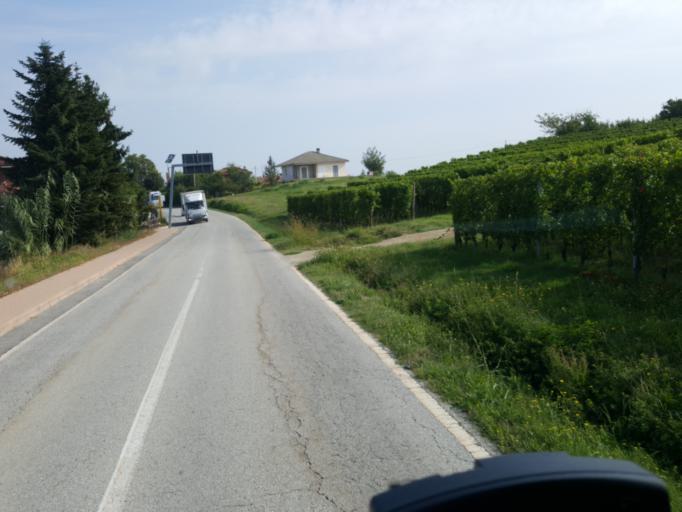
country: IT
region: Piedmont
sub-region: Provincia di Cuneo
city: Novello
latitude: 44.5953
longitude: 7.9311
